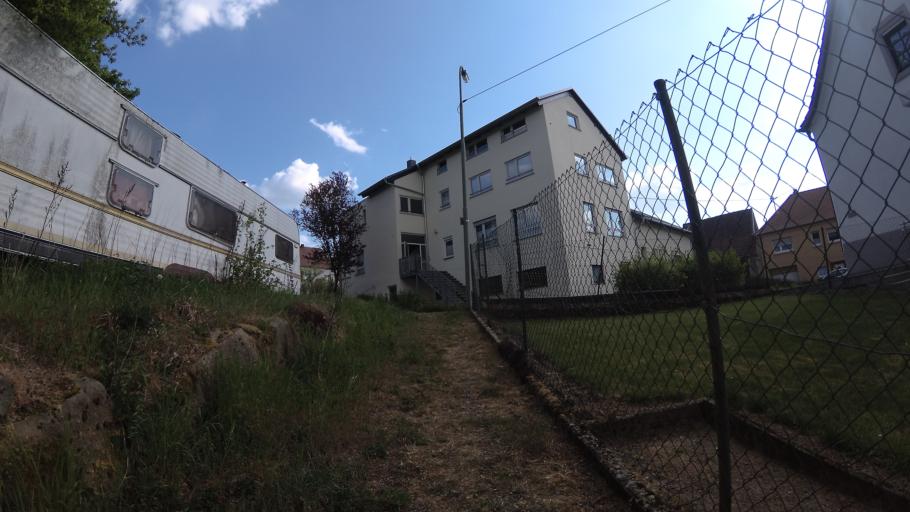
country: DE
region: Rheinland-Pfalz
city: Selchenbach
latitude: 49.4929
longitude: 7.2670
